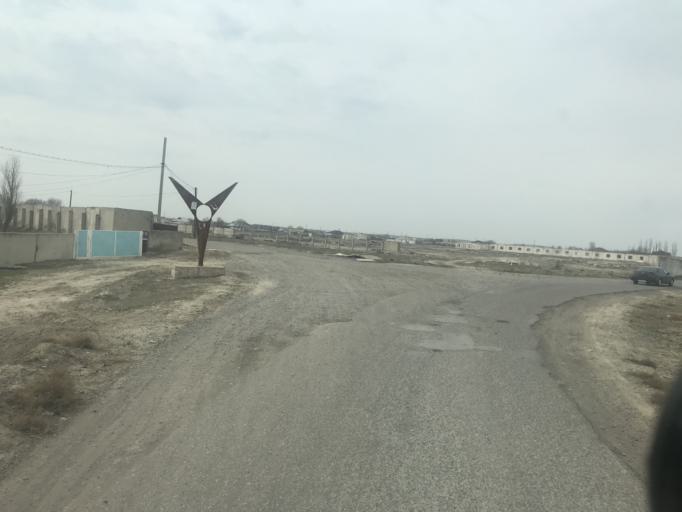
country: KZ
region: Ongtustik Qazaqstan
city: Shardara
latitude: 41.2625
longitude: 67.9462
